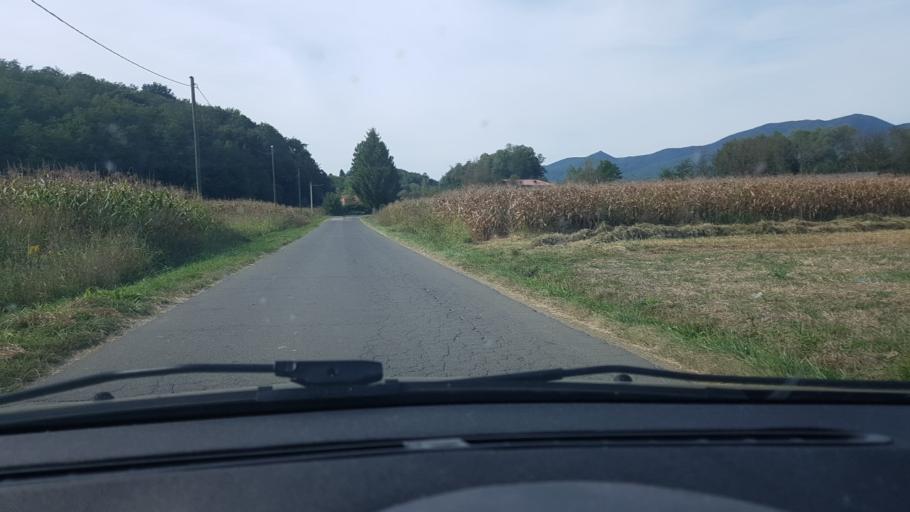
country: HR
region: Krapinsko-Zagorska
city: Zlatar
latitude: 46.1132
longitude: 16.1164
